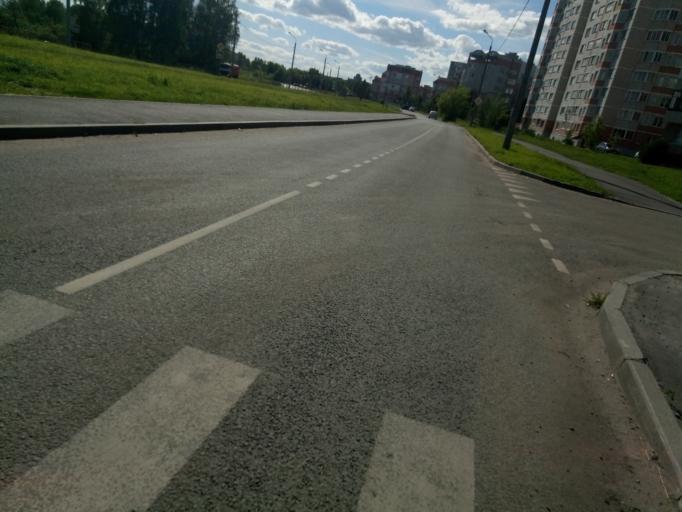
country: RU
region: Jaroslavl
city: Yaroslavl
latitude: 57.6378
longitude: 39.9561
